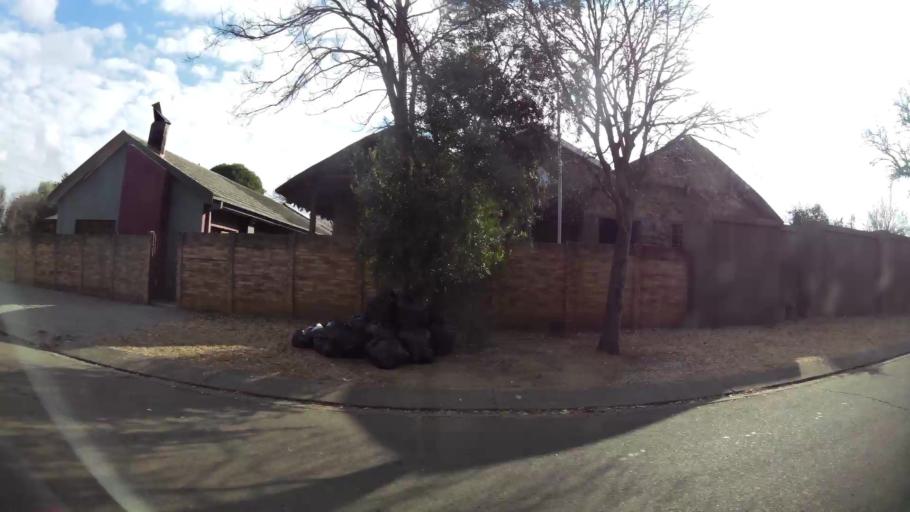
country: ZA
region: Orange Free State
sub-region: Mangaung Metropolitan Municipality
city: Bloemfontein
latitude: -29.0796
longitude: 26.2130
